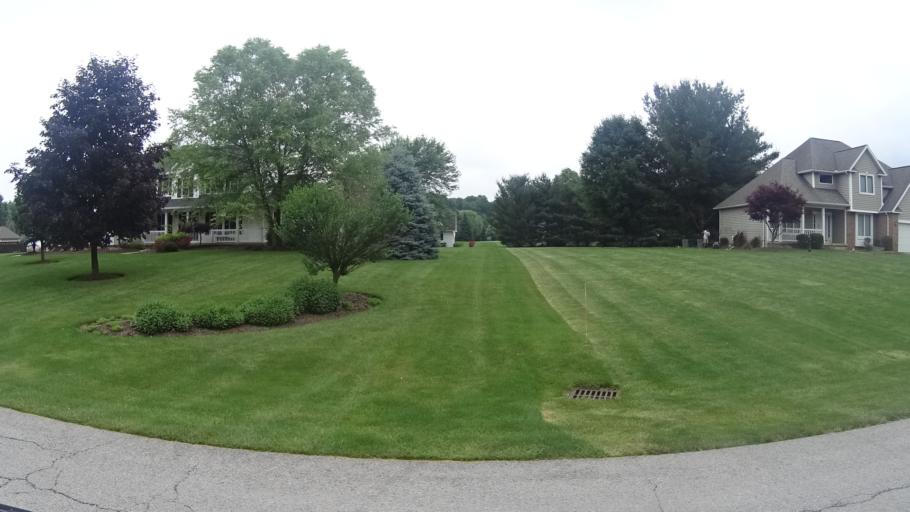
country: US
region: Ohio
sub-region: Erie County
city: Milan
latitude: 41.3018
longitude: -82.5839
